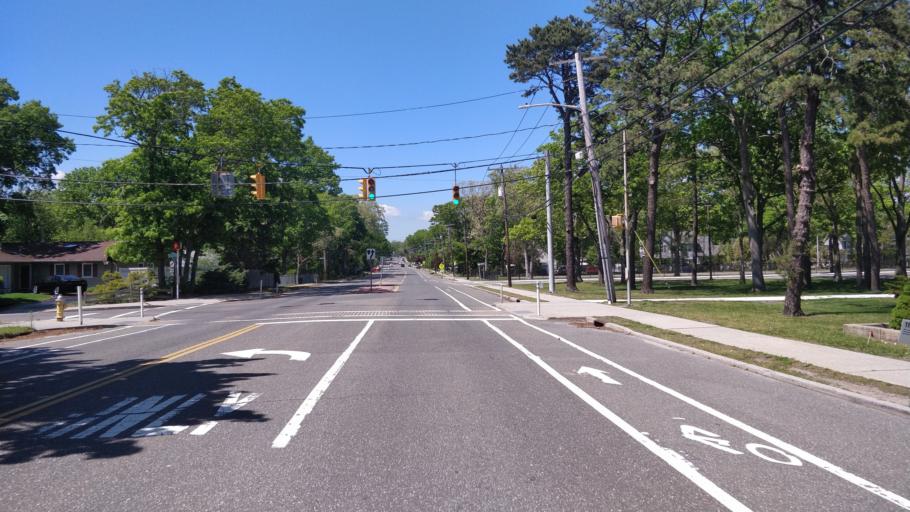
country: US
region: New York
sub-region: Suffolk County
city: Holbrook
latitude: 40.8202
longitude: -73.0945
